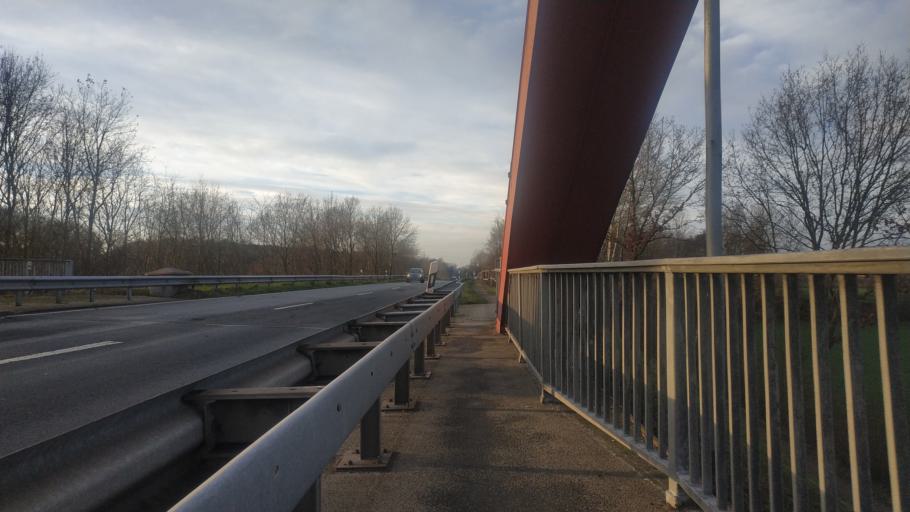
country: DE
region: North Rhine-Westphalia
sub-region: Regierungsbezirk Munster
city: Horstel
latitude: 52.2895
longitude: 7.6079
